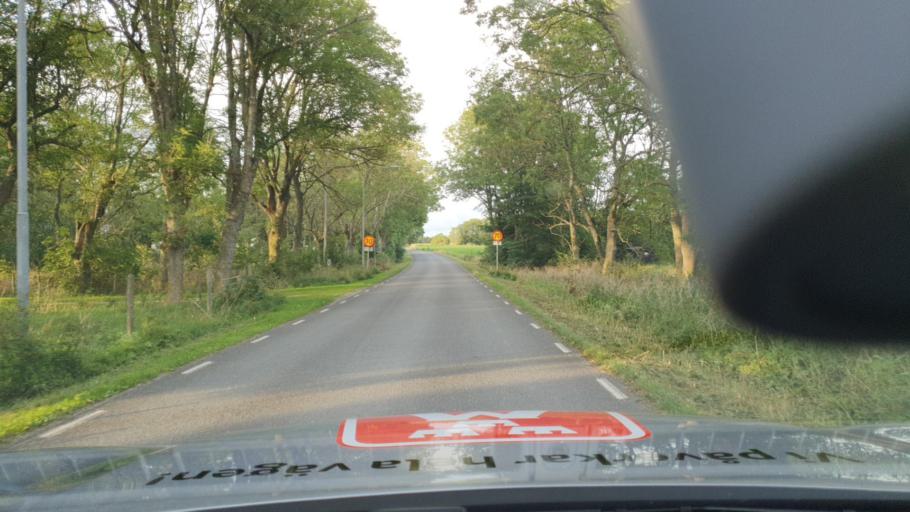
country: SE
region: Gotland
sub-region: Gotland
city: Vibble
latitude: 57.5053
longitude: 18.3074
